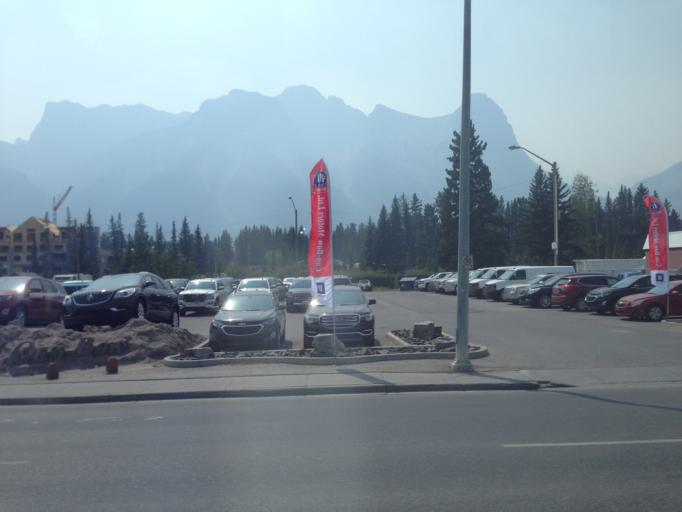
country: CA
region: Alberta
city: Canmore
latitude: 51.0885
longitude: -115.3516
